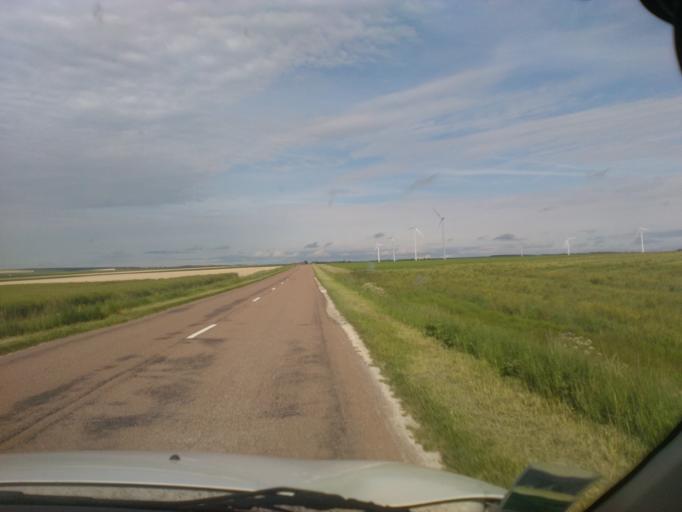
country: FR
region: Champagne-Ardenne
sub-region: Departement de l'Aube
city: Payns
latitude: 48.3646
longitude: 3.9589
